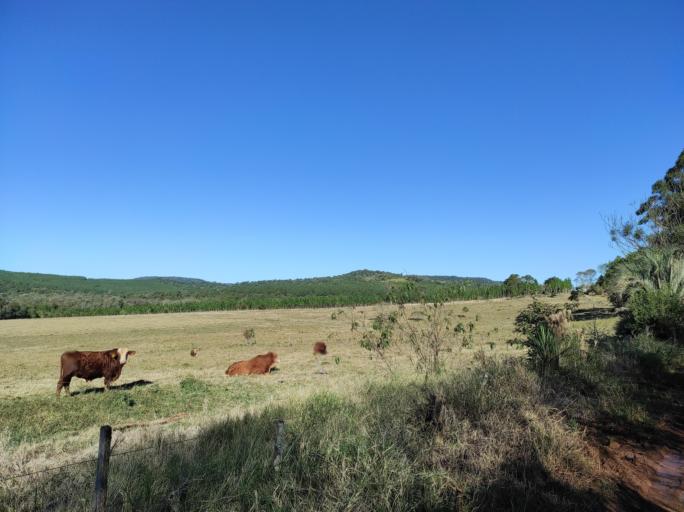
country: AR
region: Misiones
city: Capiovi
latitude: -26.9353
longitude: -54.9827
